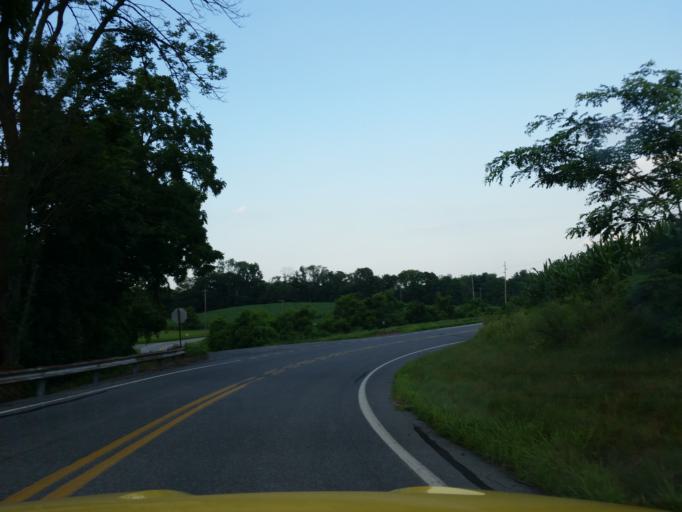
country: US
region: Pennsylvania
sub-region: Lebanon County
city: Palmyra
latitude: 40.3990
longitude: -76.6291
